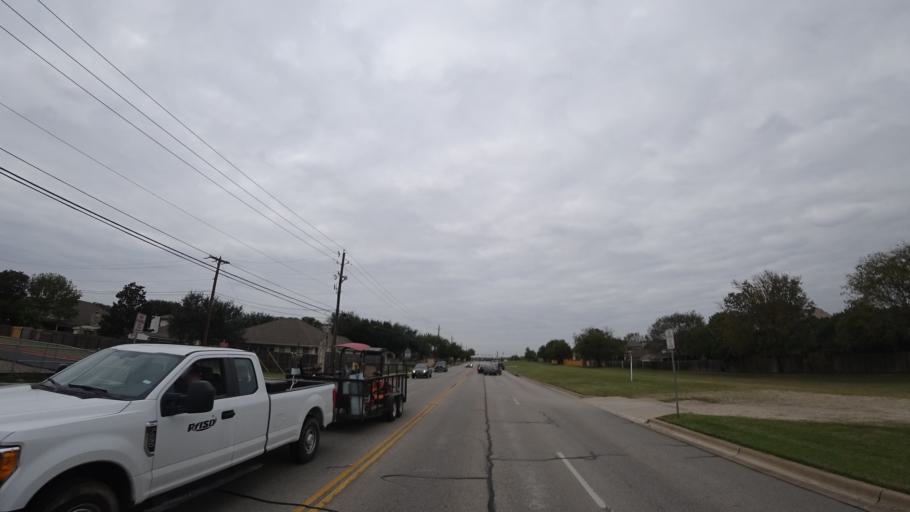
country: US
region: Texas
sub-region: Travis County
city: Pflugerville
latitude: 30.4529
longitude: -97.6171
